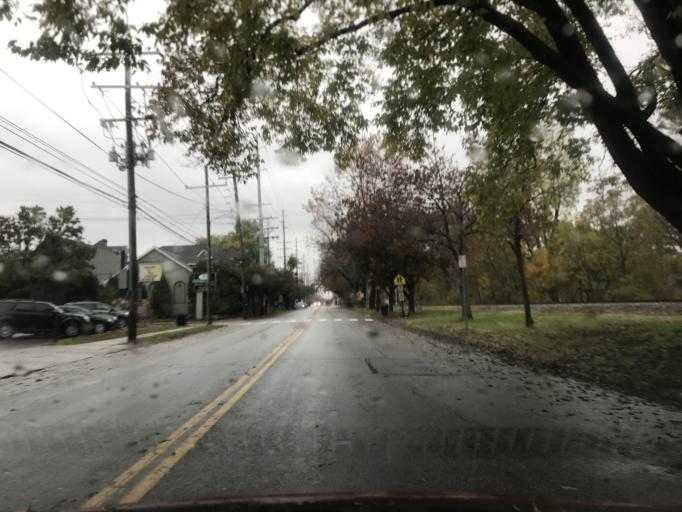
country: US
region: Kentucky
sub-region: Jefferson County
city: Indian Hills
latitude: 38.2541
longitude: -85.6975
